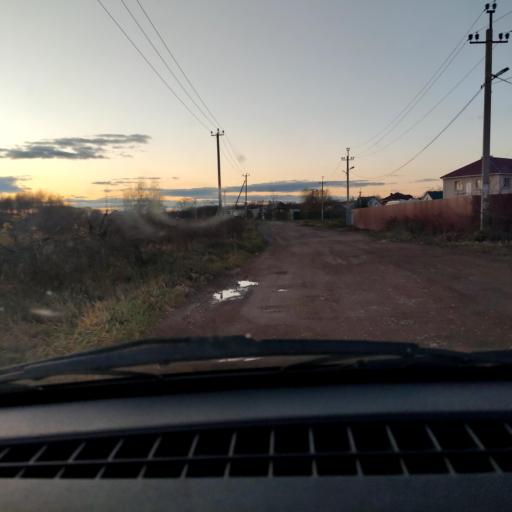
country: RU
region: Bashkortostan
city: Ufa
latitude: 54.6440
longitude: 55.9158
